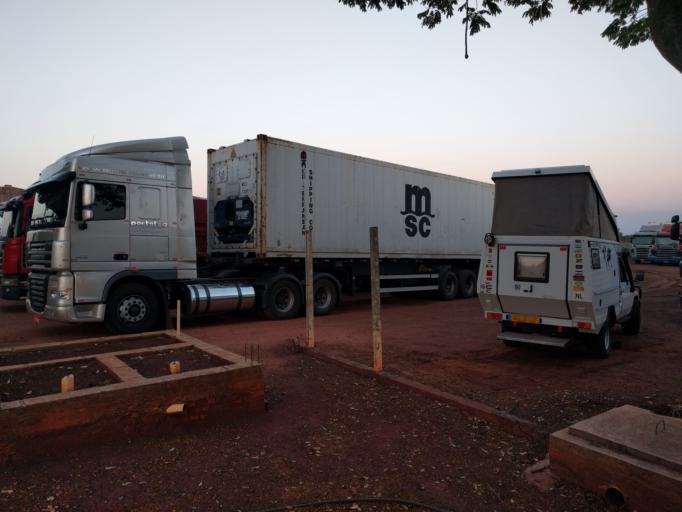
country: BR
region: Sao Paulo
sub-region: Palmital
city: Palmital
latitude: -22.7162
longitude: -50.2532
